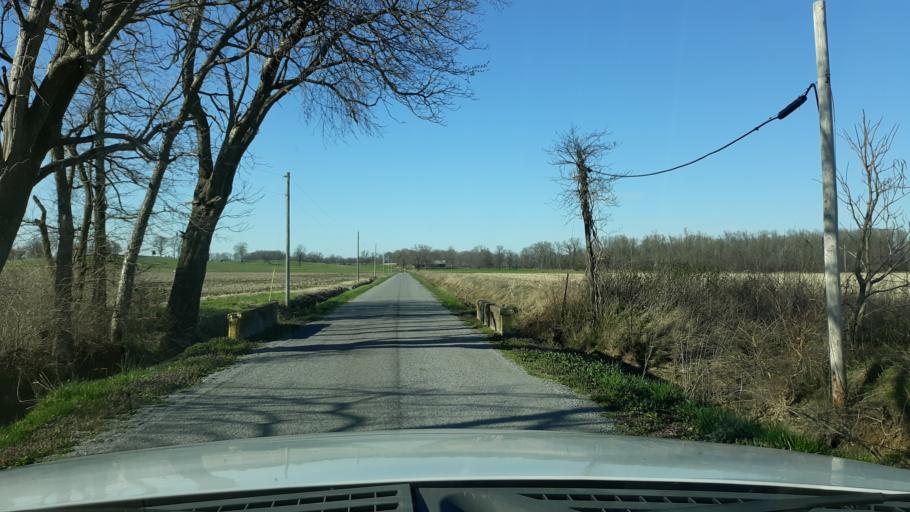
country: US
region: Illinois
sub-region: Saline County
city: Harrisburg
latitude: 37.7717
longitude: -88.5864
